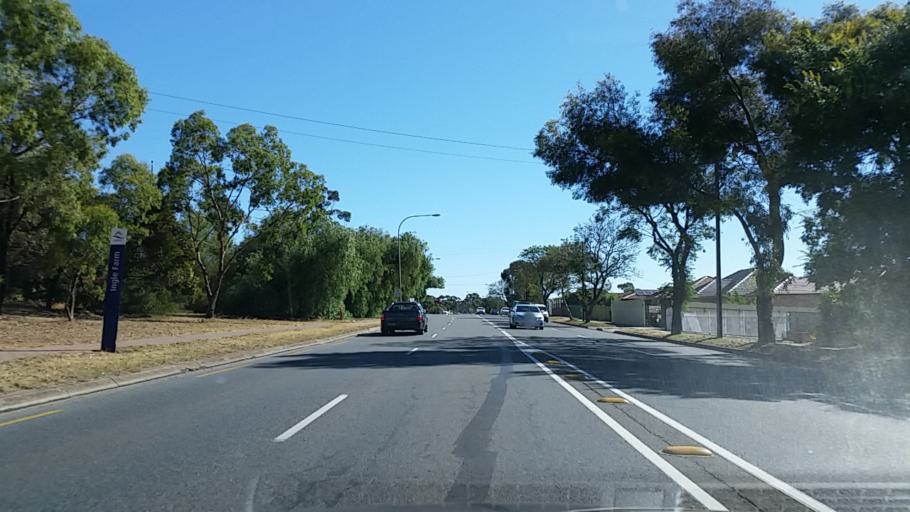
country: AU
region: South Australia
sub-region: Salisbury
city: Ingle Farm
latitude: -34.8326
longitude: 138.6282
